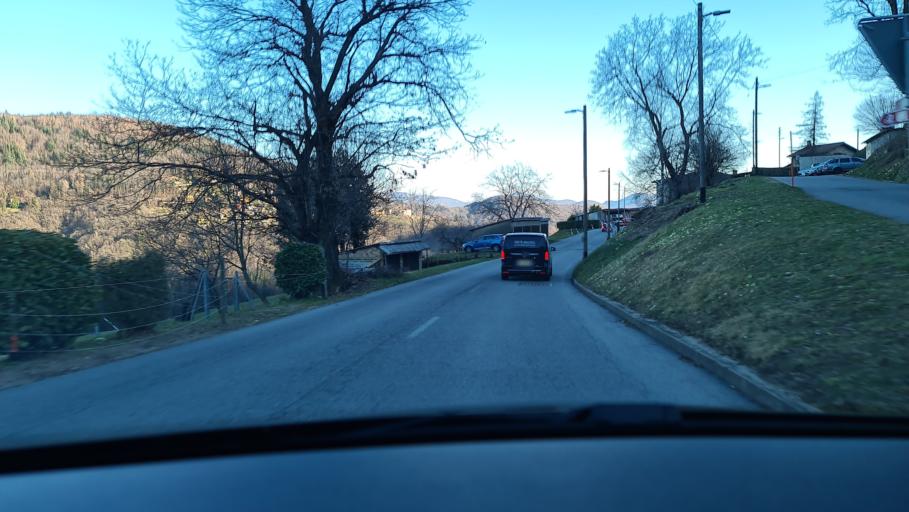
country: CH
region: Ticino
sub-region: Lugano District
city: Pura
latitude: 46.0261
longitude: 8.8582
